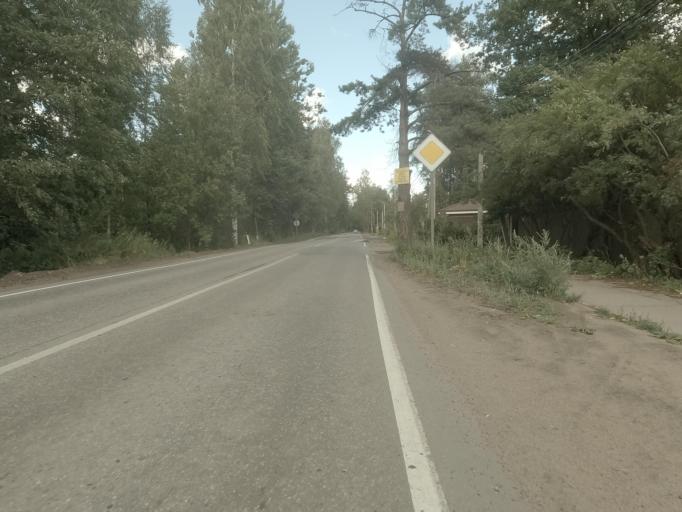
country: RU
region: Leningrad
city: Vsevolozhsk
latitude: 60.0195
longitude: 30.6849
